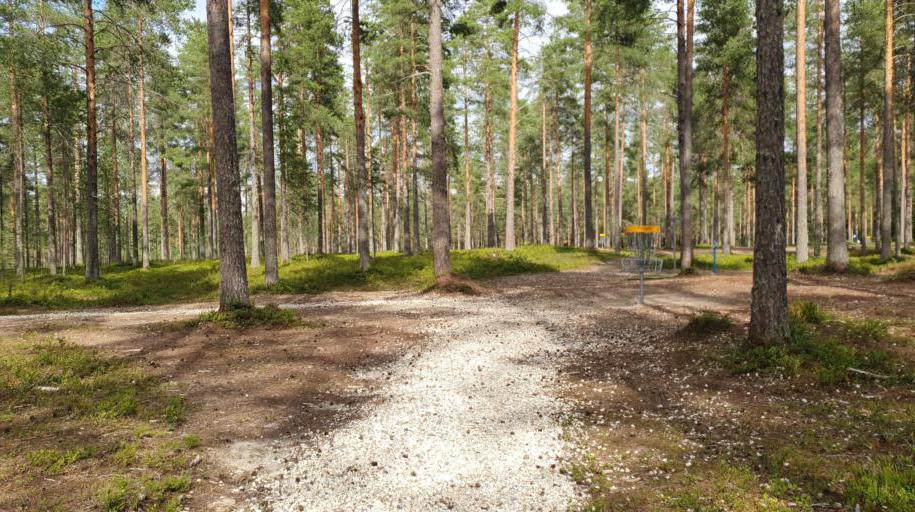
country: FI
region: Kainuu
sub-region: Kehys-Kainuu
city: Kuhmo
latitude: 64.1302
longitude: 29.5394
